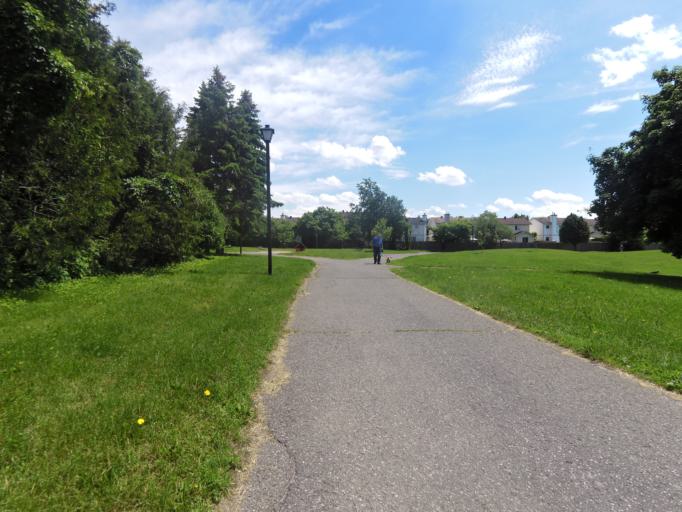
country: CA
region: Ontario
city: Ottawa
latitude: 45.3655
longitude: -75.6245
